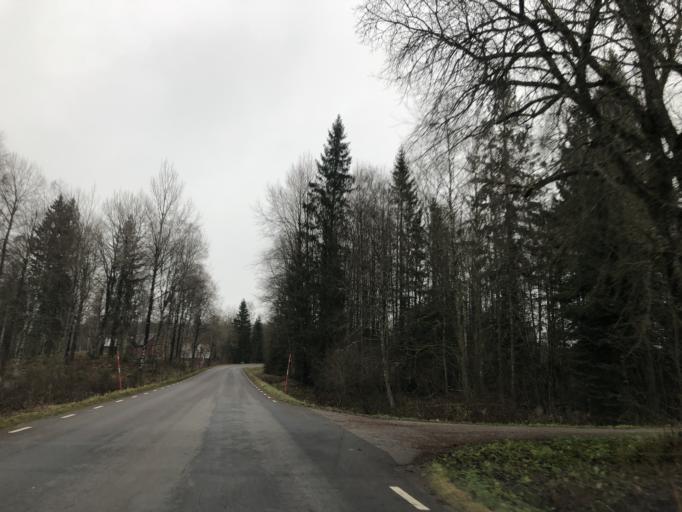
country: SE
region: Vaestra Goetaland
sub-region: Ulricehamns Kommun
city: Ulricehamn
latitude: 57.7661
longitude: 13.4669
